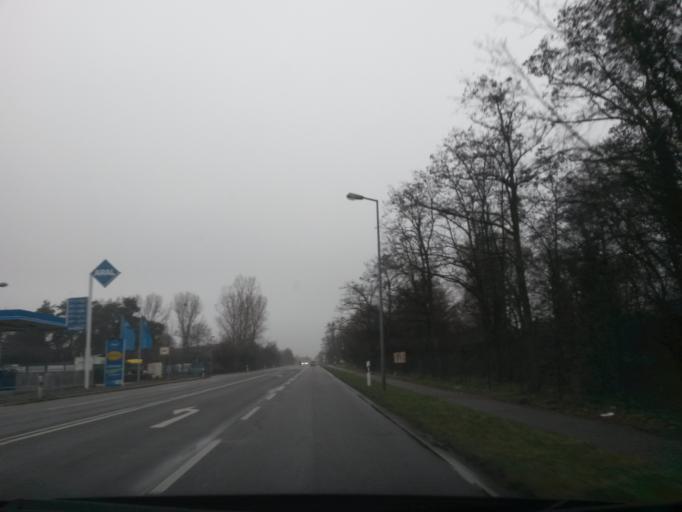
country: DE
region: Baden-Wuerttemberg
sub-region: Karlsruhe Region
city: Karlsruhe
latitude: 49.0378
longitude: 8.3943
